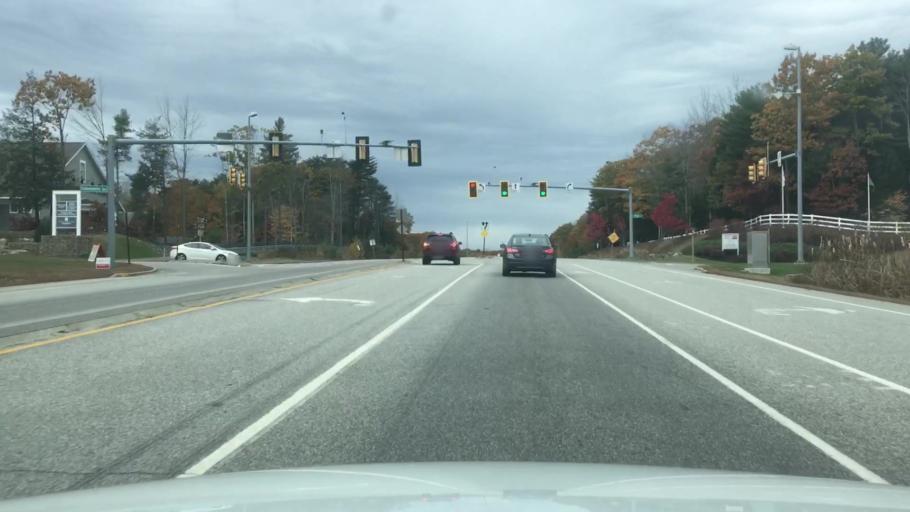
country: US
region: Maine
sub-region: Sagadahoc County
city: Topsham
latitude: 43.9358
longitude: -69.9560
